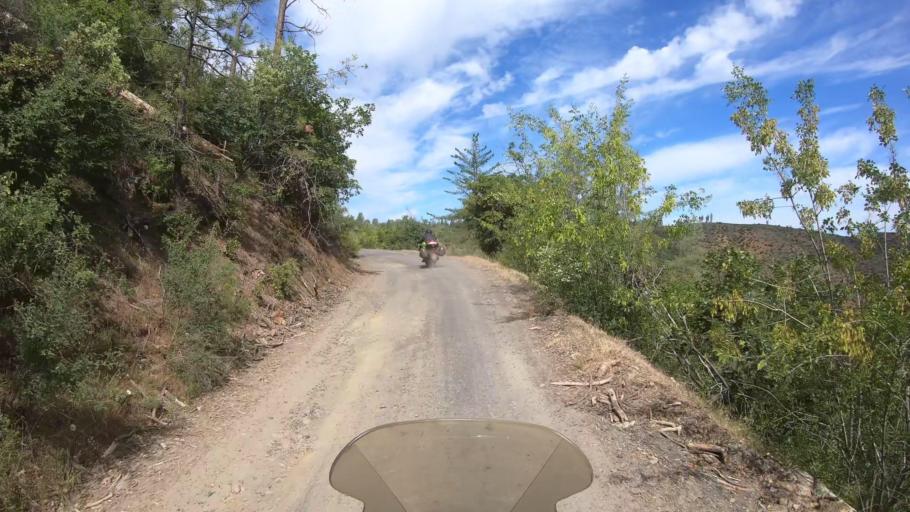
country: US
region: California
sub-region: Tuolumne County
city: Tuolumne City
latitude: 37.8333
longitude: -120.1129
